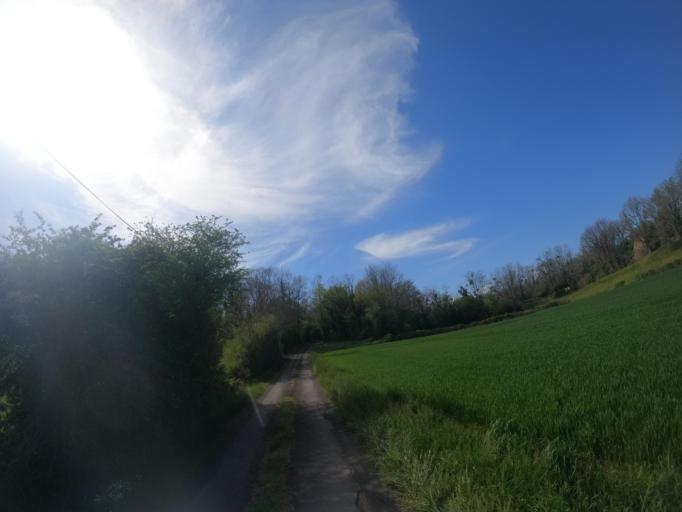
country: FR
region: Poitou-Charentes
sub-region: Departement des Deux-Sevres
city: Saint-Varent
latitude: 46.9164
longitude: -0.2032
